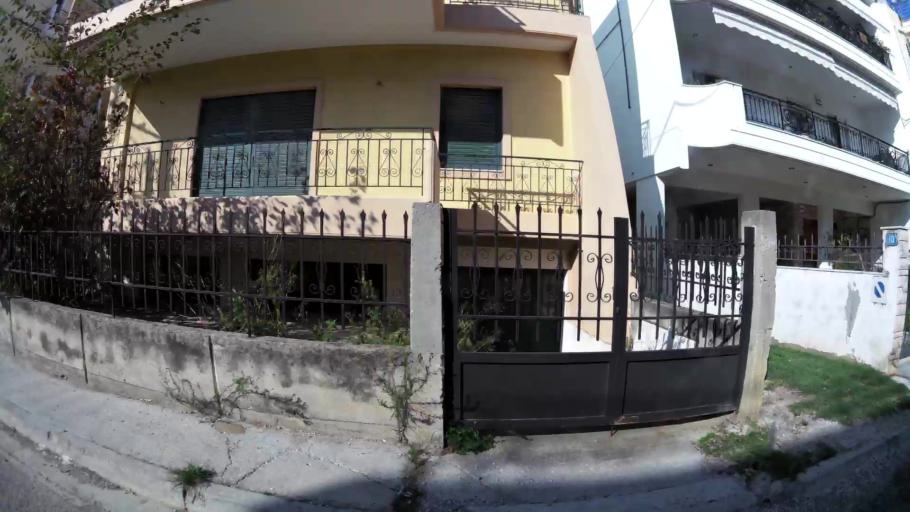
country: GR
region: Attica
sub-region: Nomarchia Anatolikis Attikis
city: Acharnes
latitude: 38.0638
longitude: 23.7400
